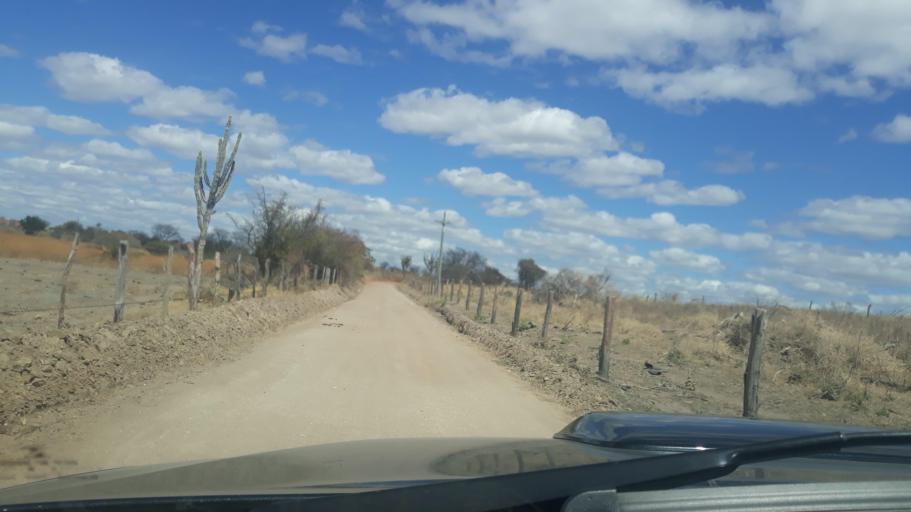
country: BR
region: Bahia
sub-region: Riacho De Santana
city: Riacho de Santana
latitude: -13.8959
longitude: -42.8494
